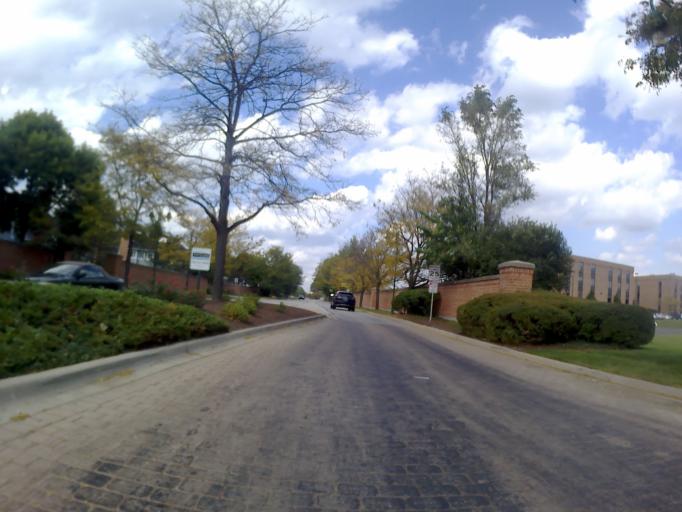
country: US
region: Illinois
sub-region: DuPage County
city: Woodridge
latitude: 41.7600
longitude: -88.0699
